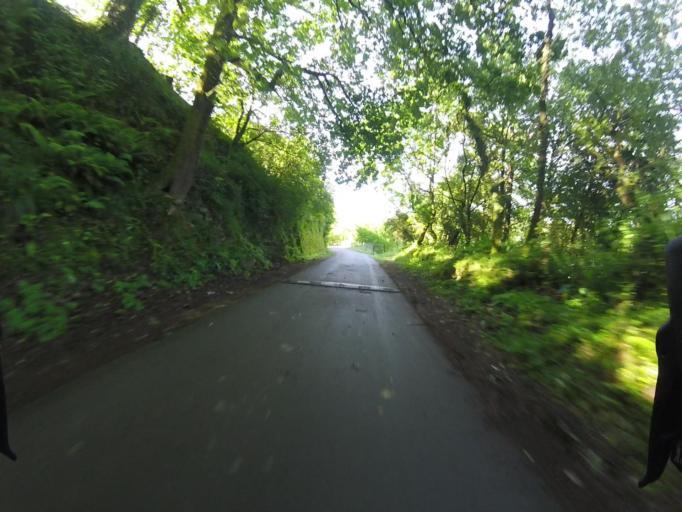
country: ES
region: Basque Country
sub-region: Provincia de Guipuzcoa
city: Andoain
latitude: 43.2114
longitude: -2.0127
